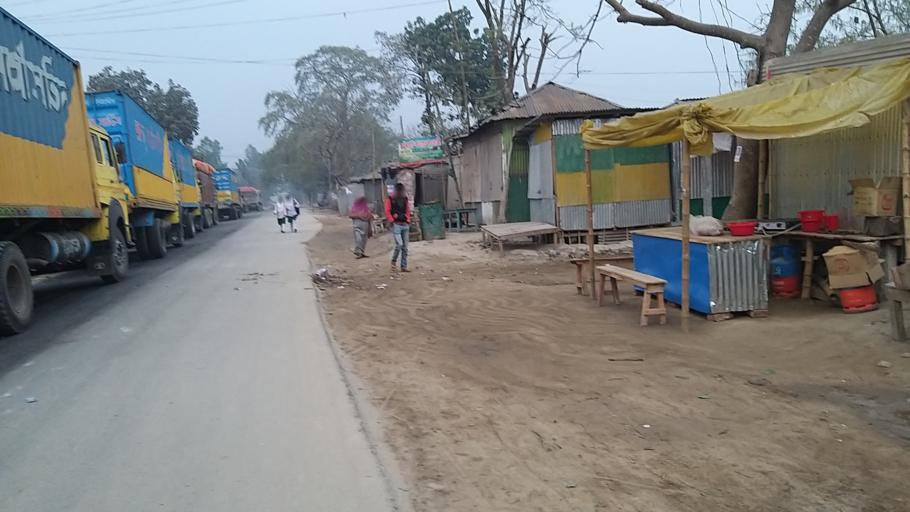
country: IN
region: West Bengal
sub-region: Koch Bihar
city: Haldibari
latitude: 26.4043
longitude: 88.9256
